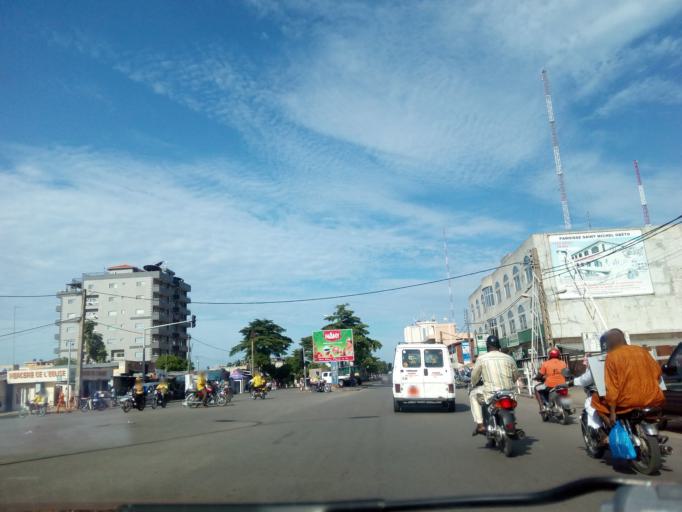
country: BJ
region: Littoral
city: Cotonou
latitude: 6.3662
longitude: 2.4286
